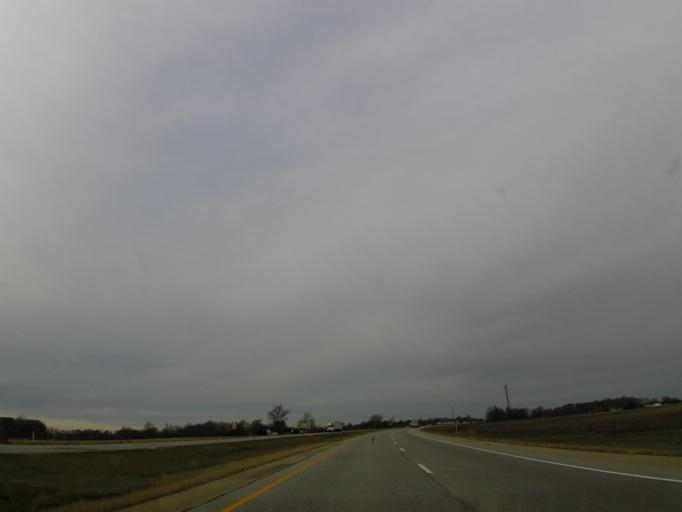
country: US
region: Indiana
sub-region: Hendricks County
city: Pittsboro
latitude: 39.8943
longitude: -86.5459
